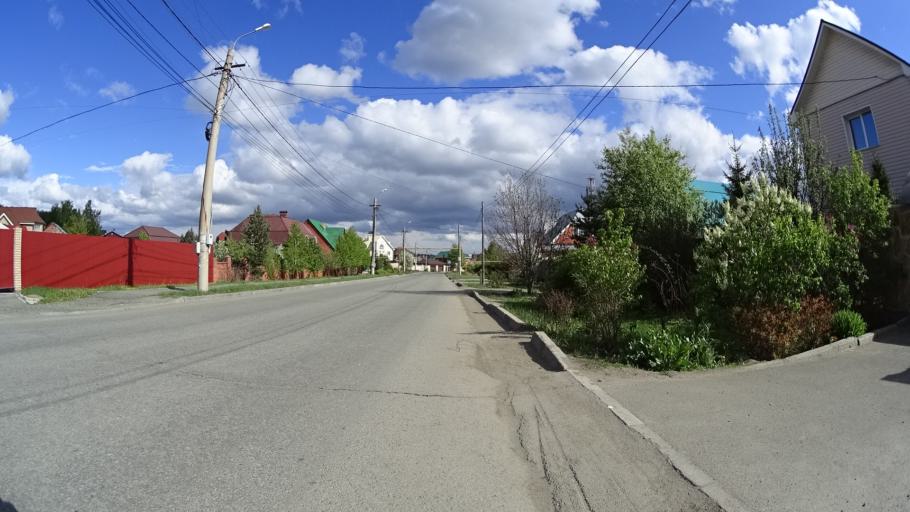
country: RU
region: Chelyabinsk
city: Sargazy
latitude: 55.1553
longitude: 61.2527
